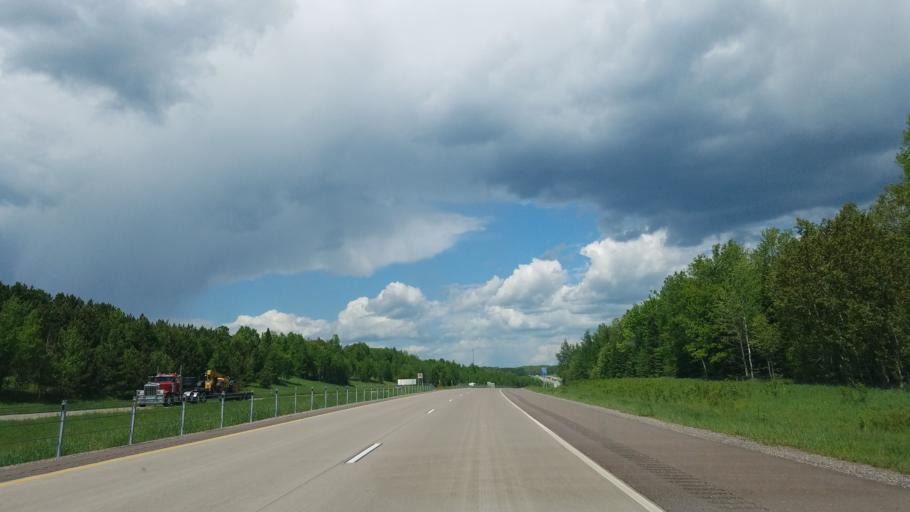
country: US
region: Minnesota
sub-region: Carlton County
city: Moose Lake
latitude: 46.4422
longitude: -92.7409
